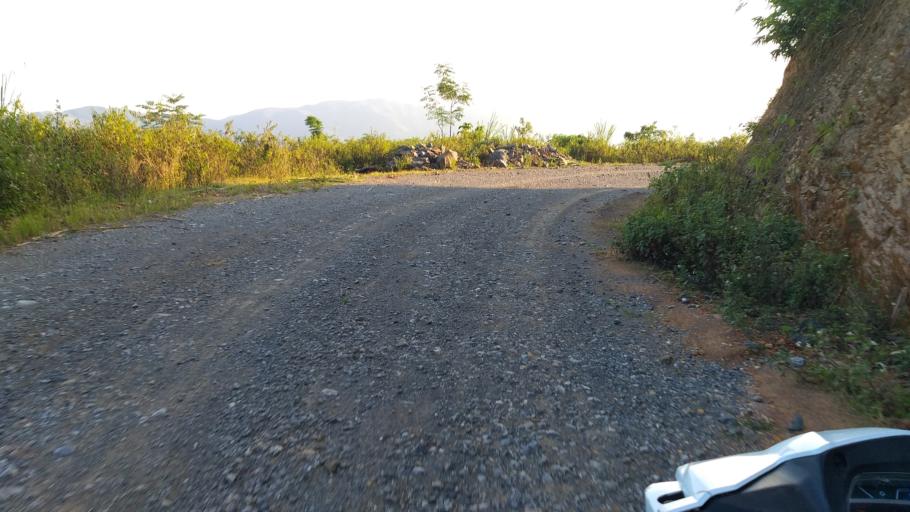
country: LA
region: Phongsali
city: Khoa
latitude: 21.1981
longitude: 102.5757
